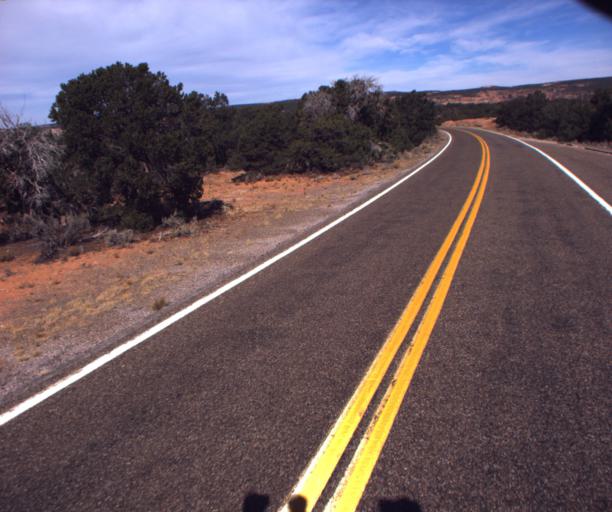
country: US
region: Arizona
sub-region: Navajo County
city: Kayenta
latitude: 36.5996
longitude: -110.4967
